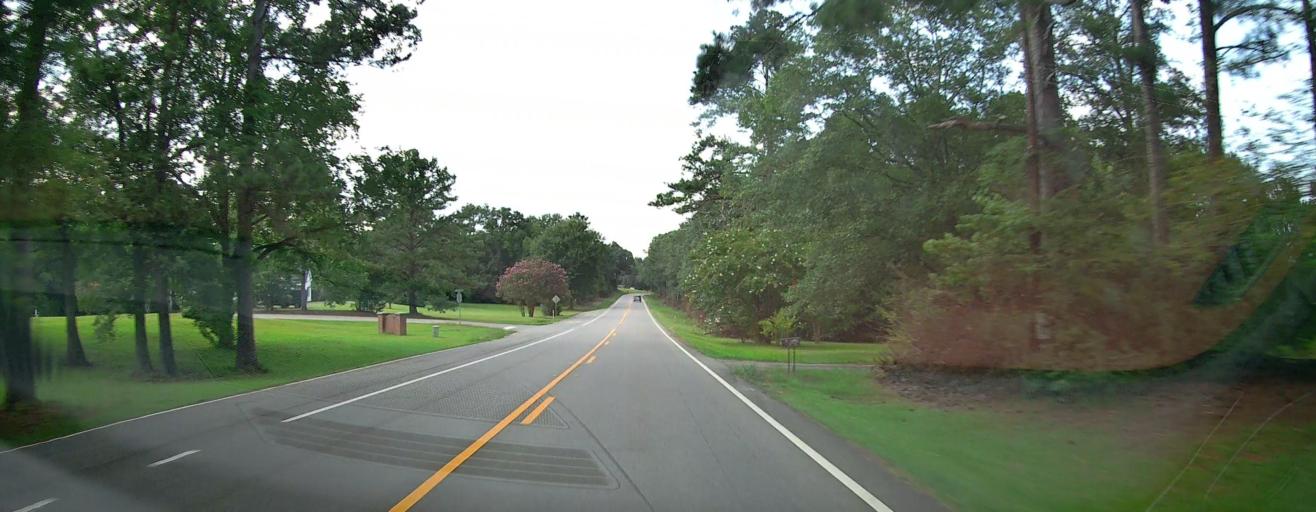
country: US
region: Georgia
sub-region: Monroe County
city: Forsyth
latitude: 33.0059
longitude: -83.9403
